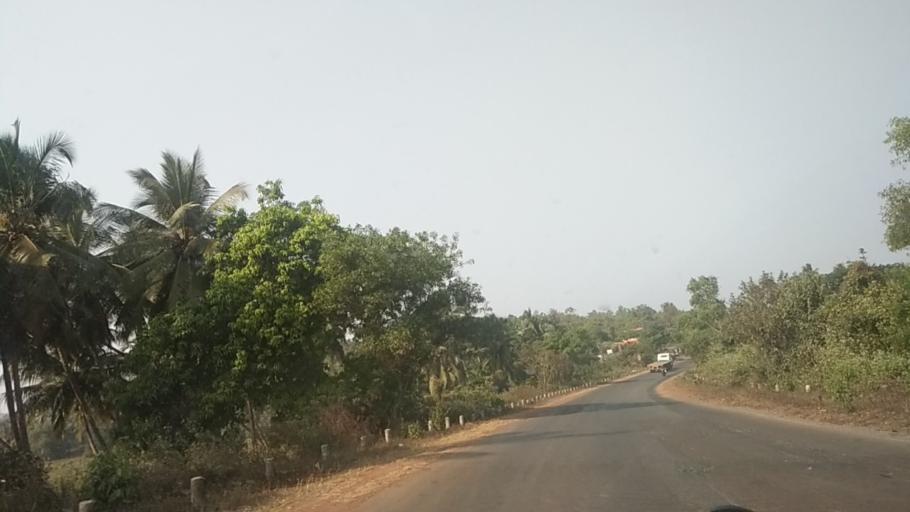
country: IN
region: Goa
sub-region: North Goa
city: Colovale
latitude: 15.6714
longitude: 73.8369
